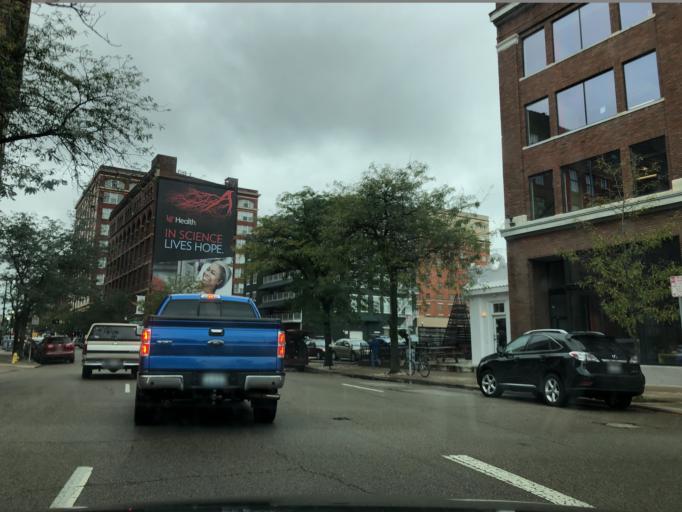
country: US
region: Kentucky
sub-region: Campbell County
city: Newport
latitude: 39.1053
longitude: -84.5074
